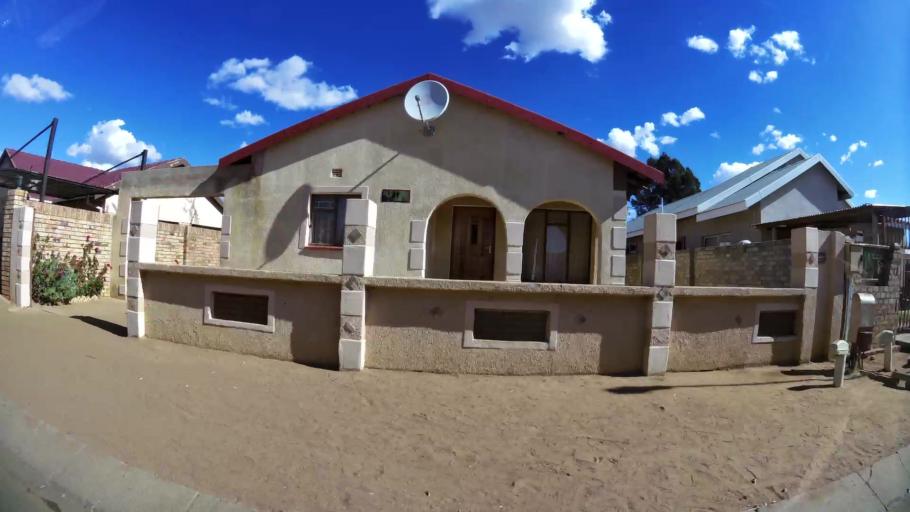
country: ZA
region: North-West
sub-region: Dr Kenneth Kaunda District Municipality
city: Klerksdorp
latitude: -26.8700
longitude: 26.5859
